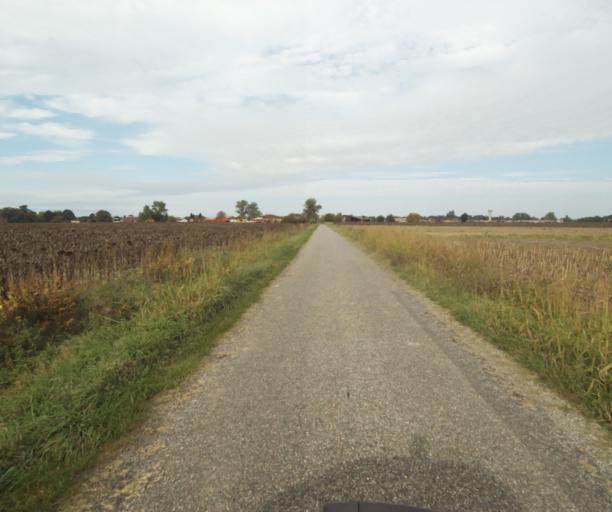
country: FR
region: Midi-Pyrenees
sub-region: Departement du Tarn-et-Garonne
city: Finhan
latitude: 43.9057
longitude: 1.2331
